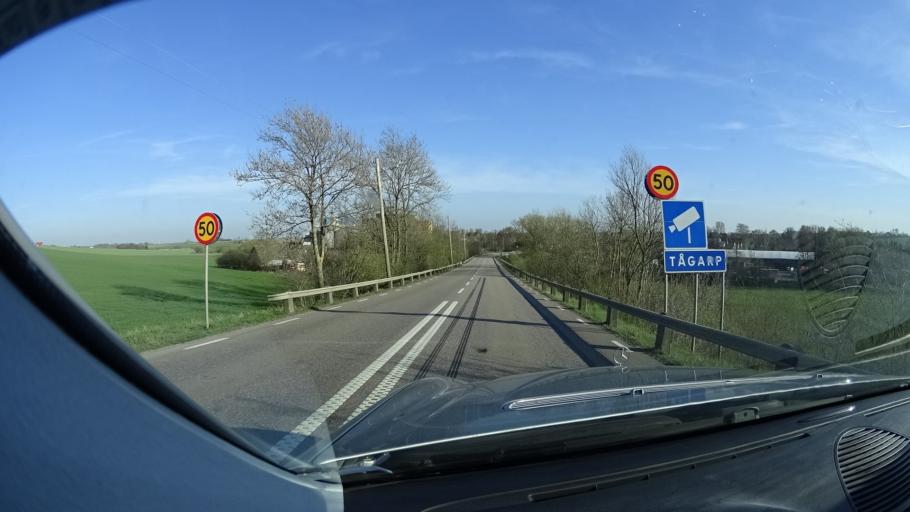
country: SE
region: Skane
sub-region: Landskrona
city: Asmundtorp
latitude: 55.9292
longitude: 12.9539
